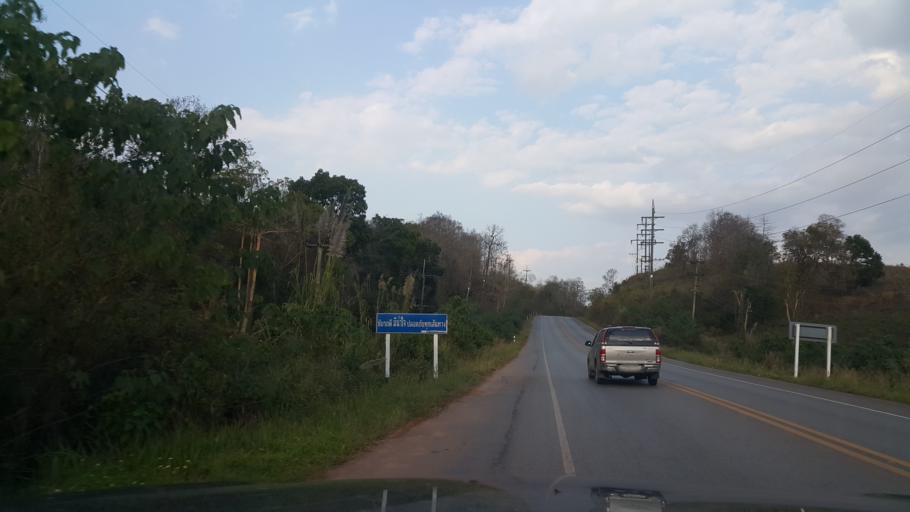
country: TH
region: Loei
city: Dan Sai
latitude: 17.3075
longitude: 101.2046
